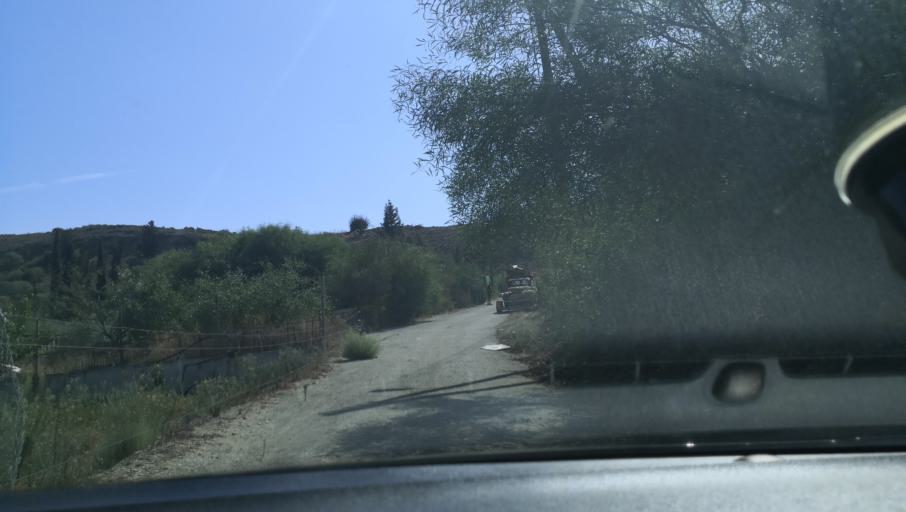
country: CY
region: Lefkosia
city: Mammari
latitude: 35.1714
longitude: 33.2061
